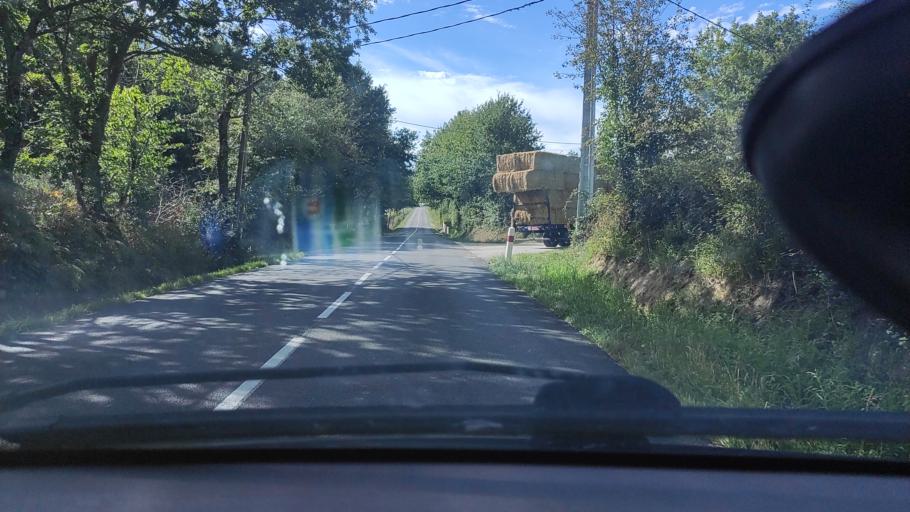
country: FR
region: Pays de la Loire
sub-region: Departement de la Vendee
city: La Boissiere-des-Landes
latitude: 46.5527
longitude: -1.4274
